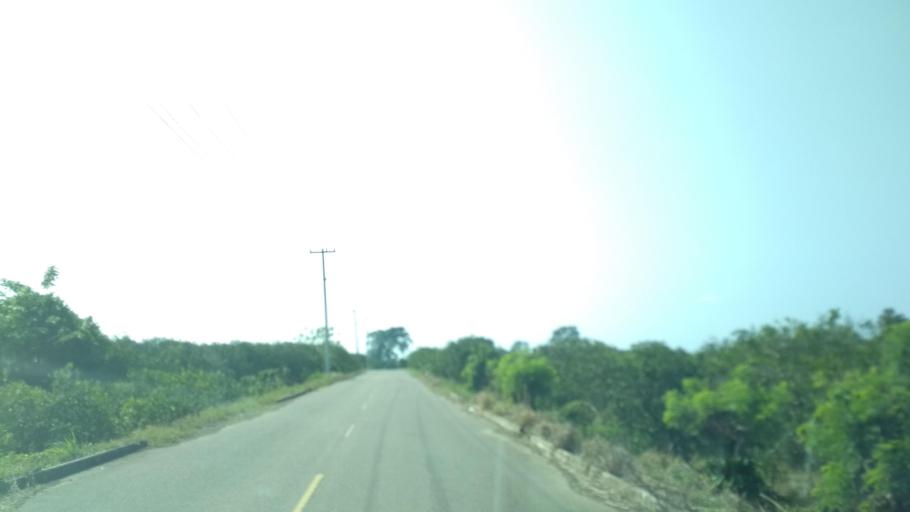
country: MX
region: Puebla
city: San Jose Acateno
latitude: 20.2045
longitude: -97.1787
